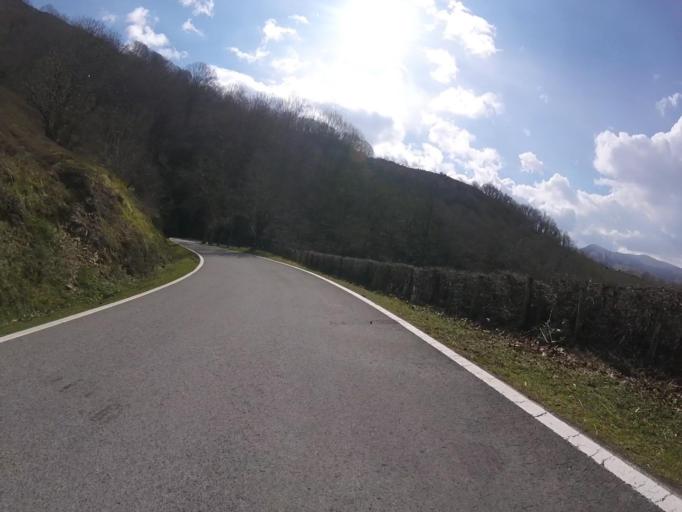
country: ES
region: Navarre
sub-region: Provincia de Navarra
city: Etxalar
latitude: 43.2513
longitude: -1.6130
